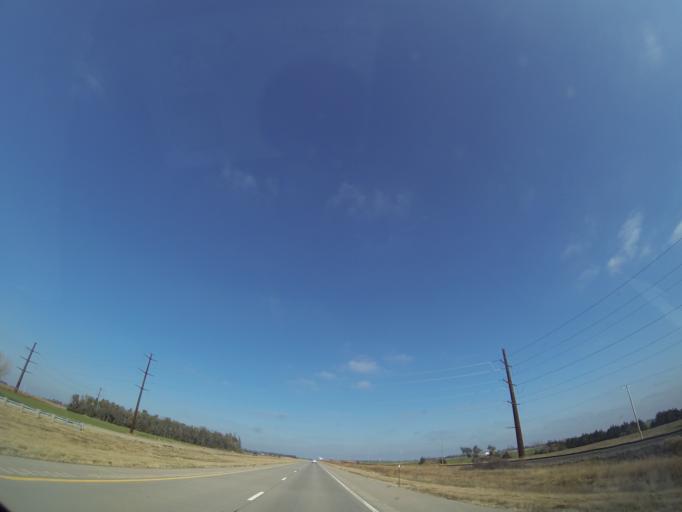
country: US
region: Kansas
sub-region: McPherson County
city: Inman
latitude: 38.2002
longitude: -97.8022
